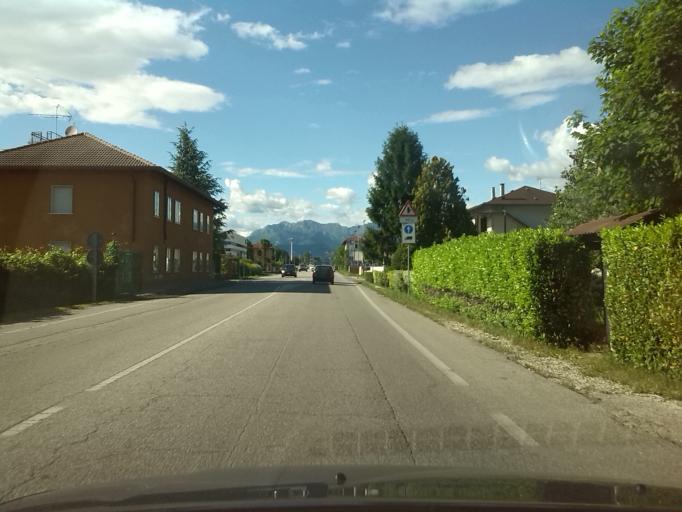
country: IT
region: Friuli Venezia Giulia
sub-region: Provincia di Udine
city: Tavagnacco
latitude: 46.1132
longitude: 13.2275
